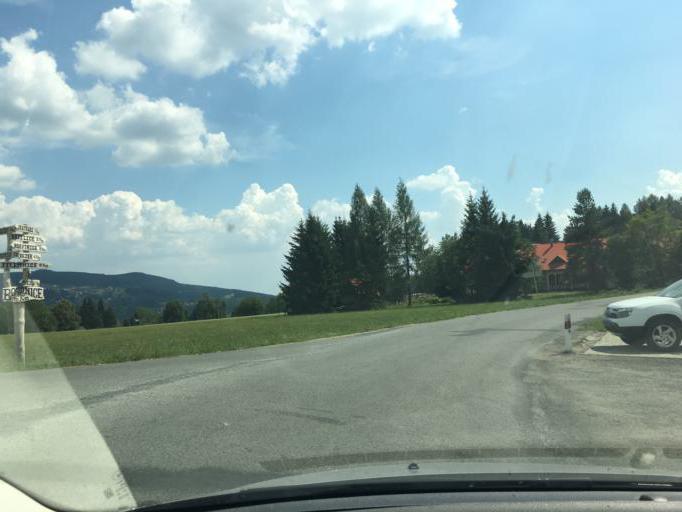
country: CZ
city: Benecko
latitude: 50.6775
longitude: 15.5084
